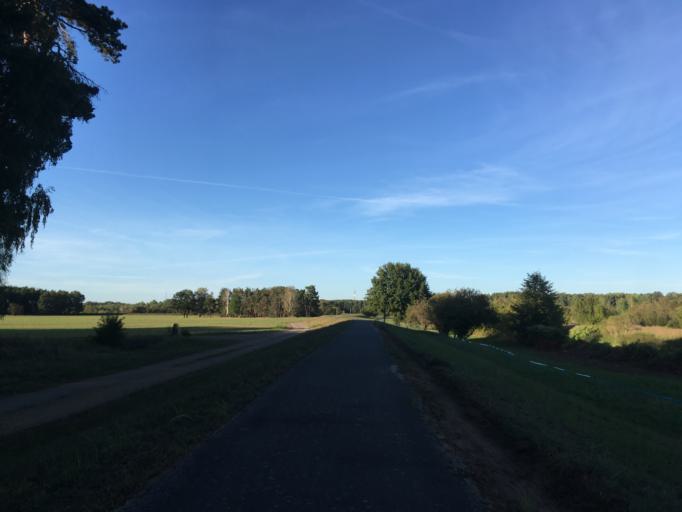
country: PL
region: Lubusz
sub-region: Powiat zarski
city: Trzebiel
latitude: 51.6572
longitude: 14.7550
